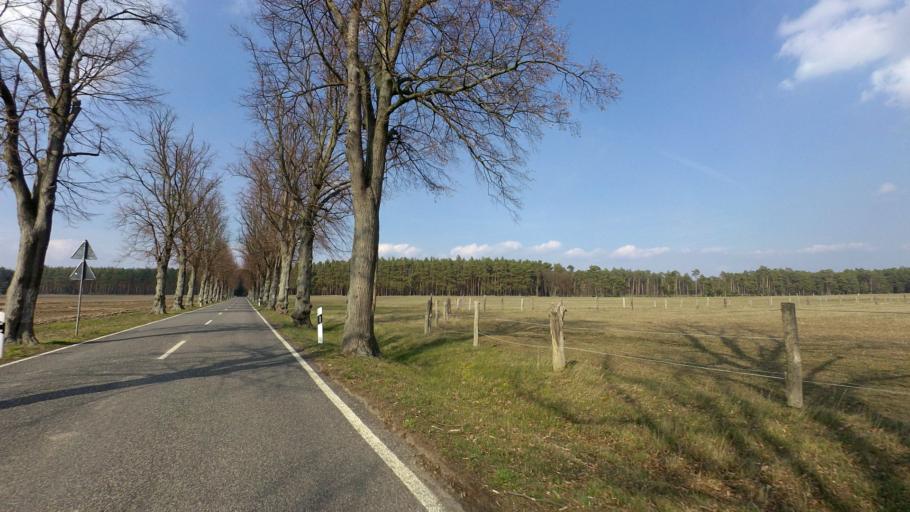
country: DE
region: Brandenburg
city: Dahme
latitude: 51.9431
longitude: 13.4422
